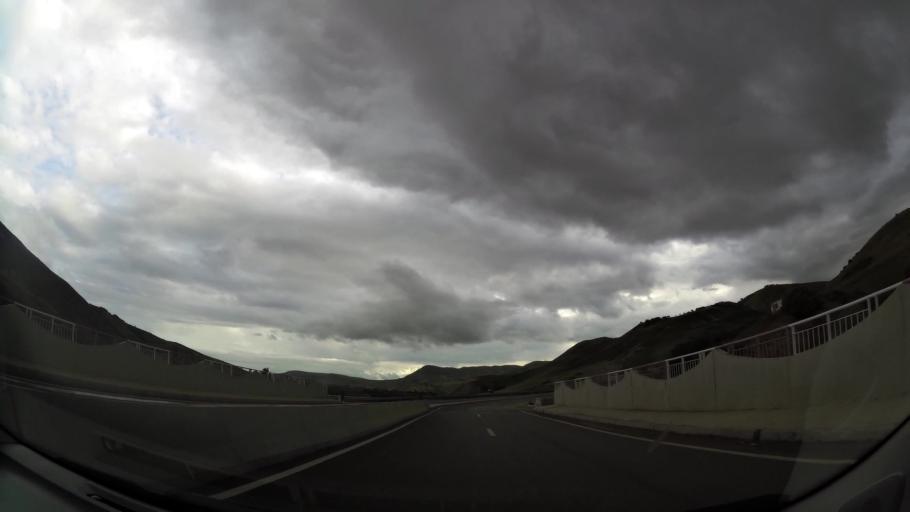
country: MA
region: Taza-Al Hoceima-Taounate
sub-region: Taza
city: Taza
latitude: 34.3217
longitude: -3.9531
